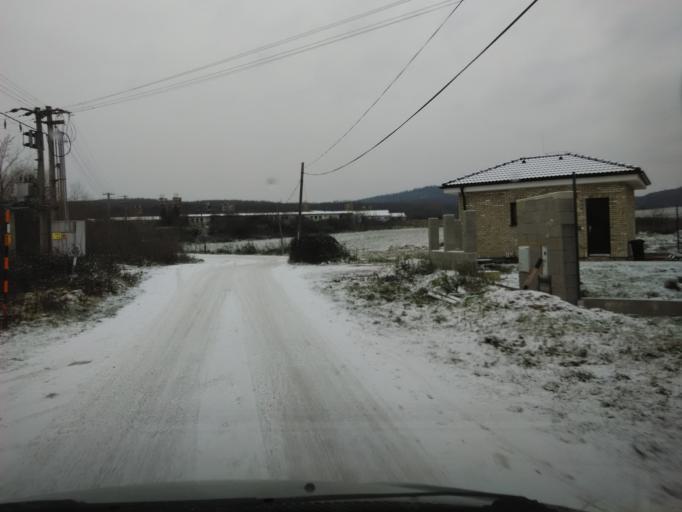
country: SK
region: Nitriansky
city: Zlate Moravce
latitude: 48.4431
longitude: 18.3595
